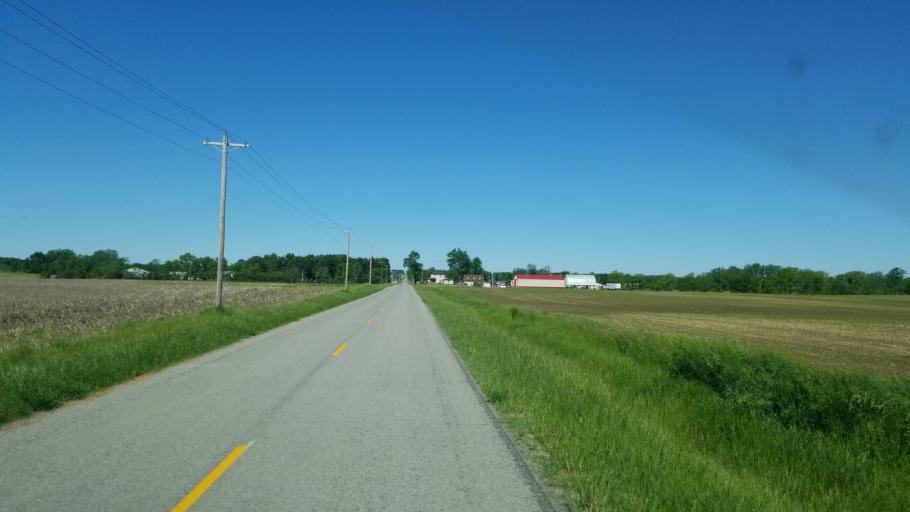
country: US
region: Ohio
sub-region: Logan County
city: Northwood
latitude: 40.4487
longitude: -83.6050
